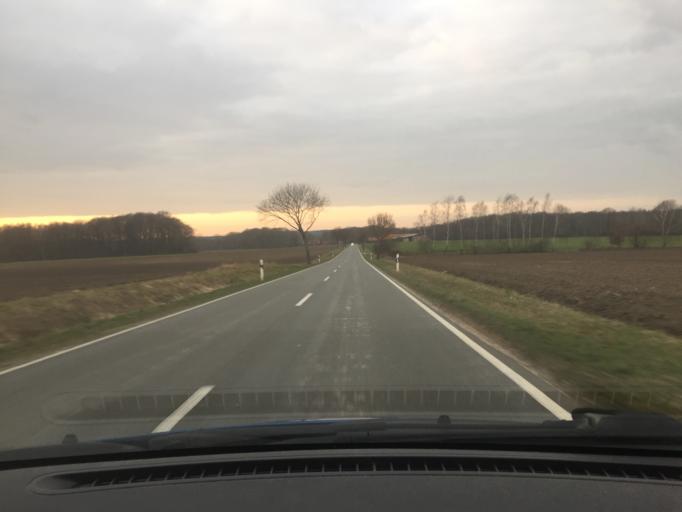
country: DE
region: Lower Saxony
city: Romstedt
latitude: 53.0524
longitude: 10.6277
